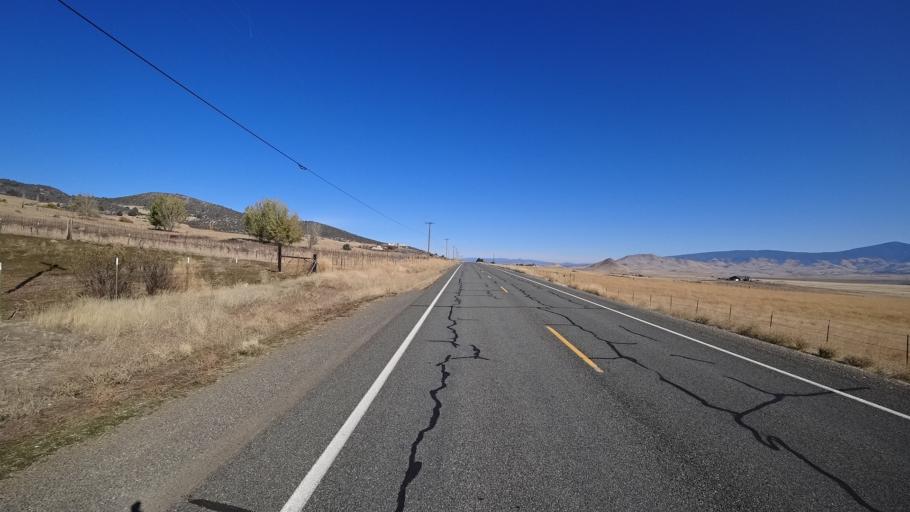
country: US
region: California
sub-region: Siskiyou County
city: Montague
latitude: 41.7925
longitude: -122.5135
